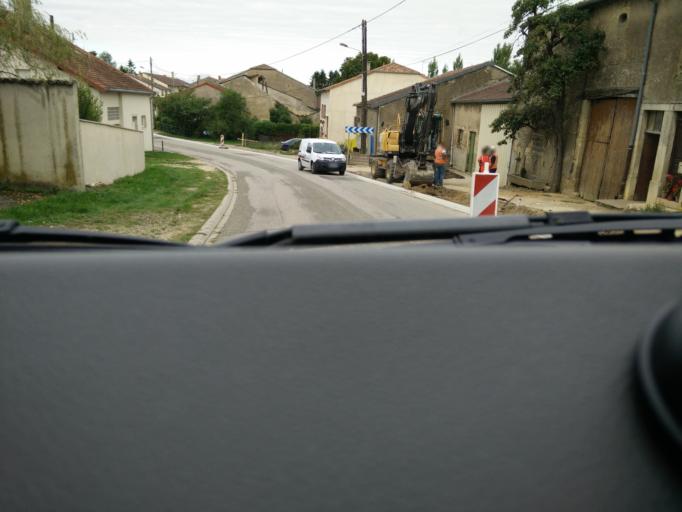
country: FR
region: Lorraine
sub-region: Departement de la Meuse
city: Vigneulles-les-Hattonchatel
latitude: 48.9621
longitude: 5.8273
